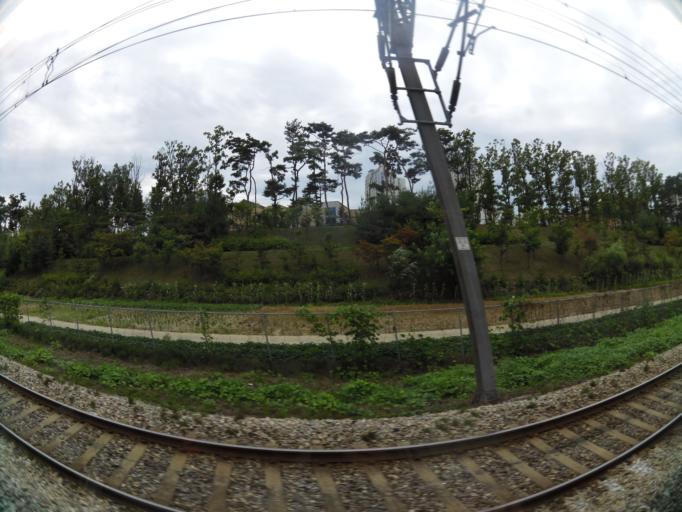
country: KR
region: Gyeonggi-do
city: Osan
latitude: 37.1788
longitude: 127.0544
